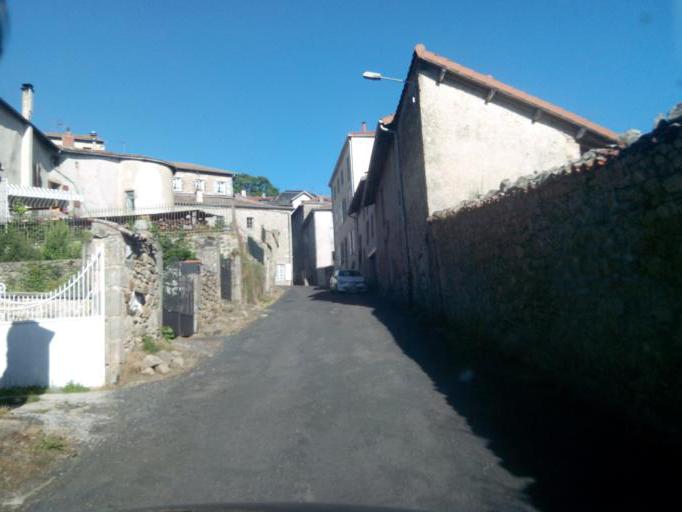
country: FR
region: Auvergne
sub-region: Departement de la Haute-Loire
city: Fontannes
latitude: 45.3206
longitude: 3.6944
